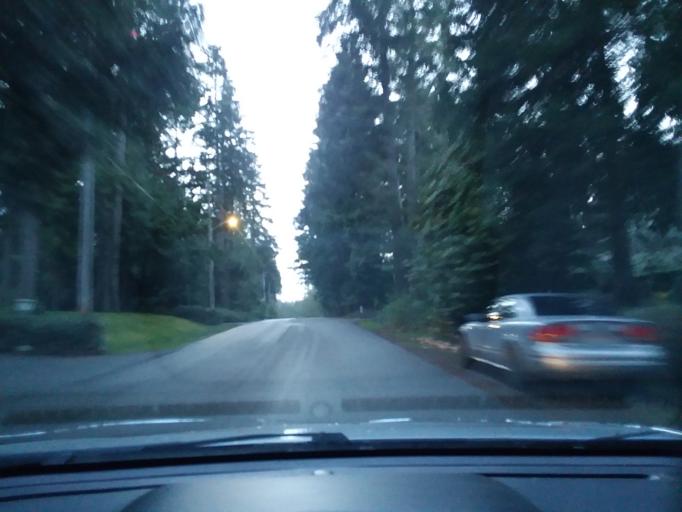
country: US
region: Washington
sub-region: King County
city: Lake Forest Park
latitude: 47.7608
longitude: -122.2934
